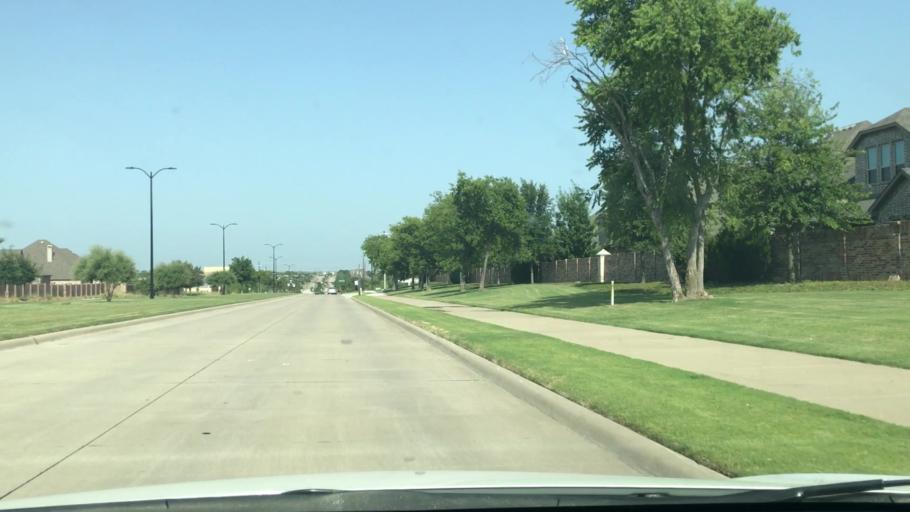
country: US
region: Texas
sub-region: Collin County
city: Frisco
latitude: 33.1377
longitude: -96.7551
